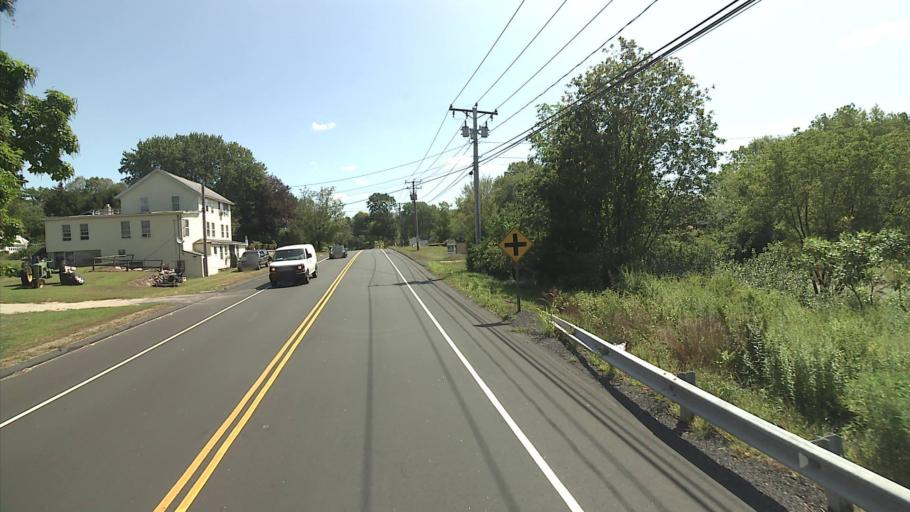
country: US
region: Connecticut
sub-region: New London County
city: Preston City
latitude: 41.5729
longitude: -71.8760
